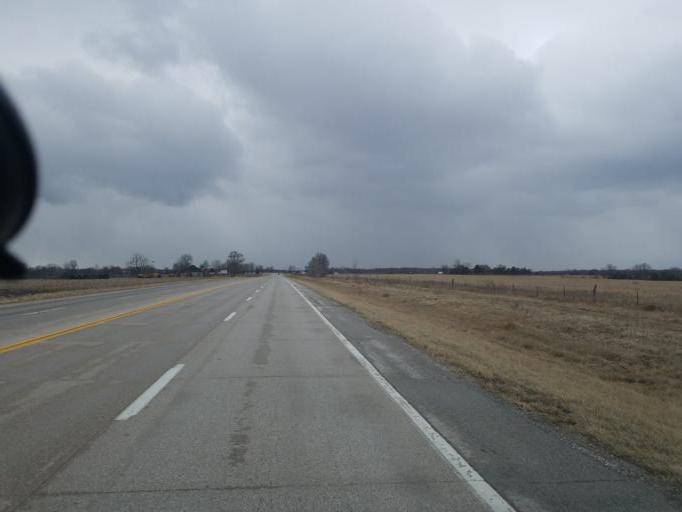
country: US
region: Missouri
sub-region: Macon County
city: Macon
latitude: 39.7953
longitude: -92.4773
